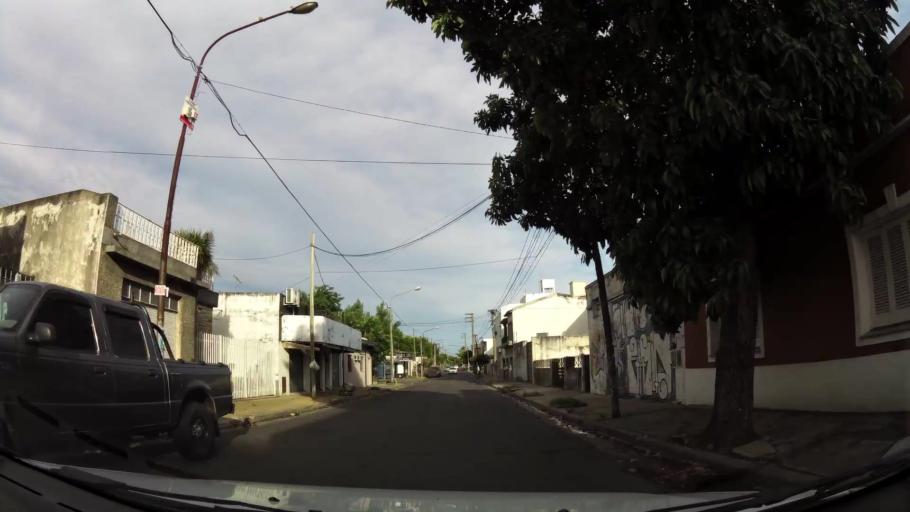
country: AR
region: Buenos Aires
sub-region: Partido de Moron
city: Moron
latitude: -34.6387
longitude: -58.6309
